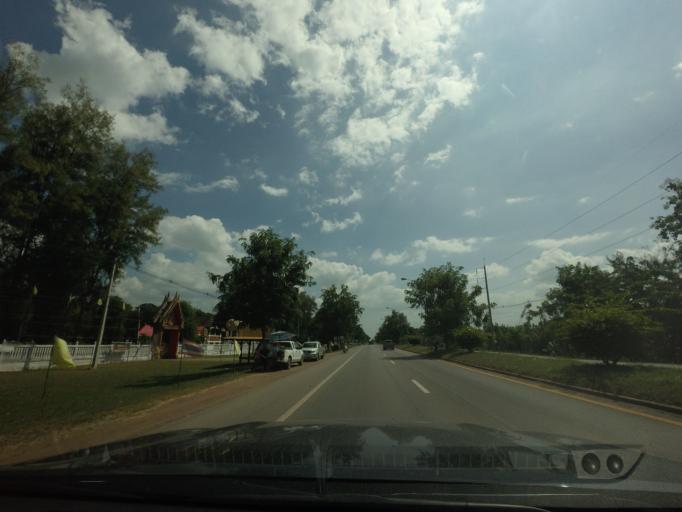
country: TH
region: Phetchabun
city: Nong Phai
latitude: 15.9101
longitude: 101.0270
